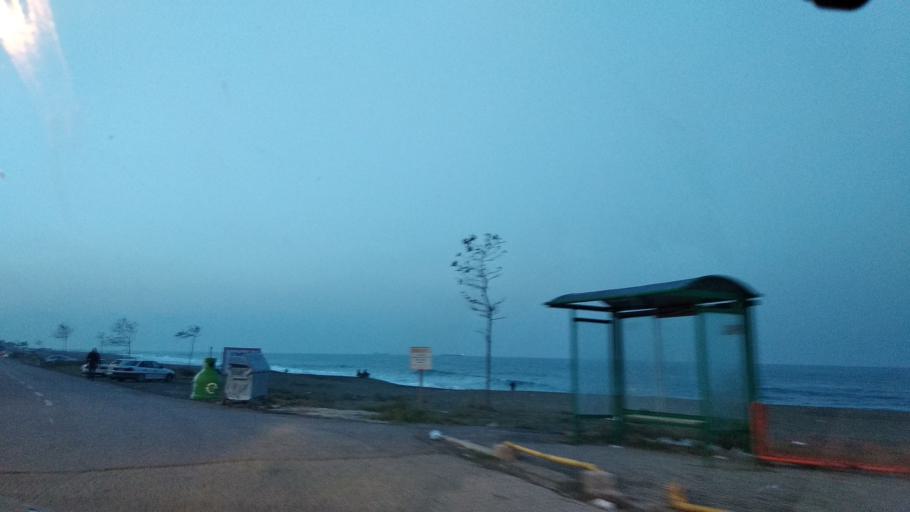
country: TR
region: Sakarya
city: Karasu
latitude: 41.0911
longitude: 30.7421
